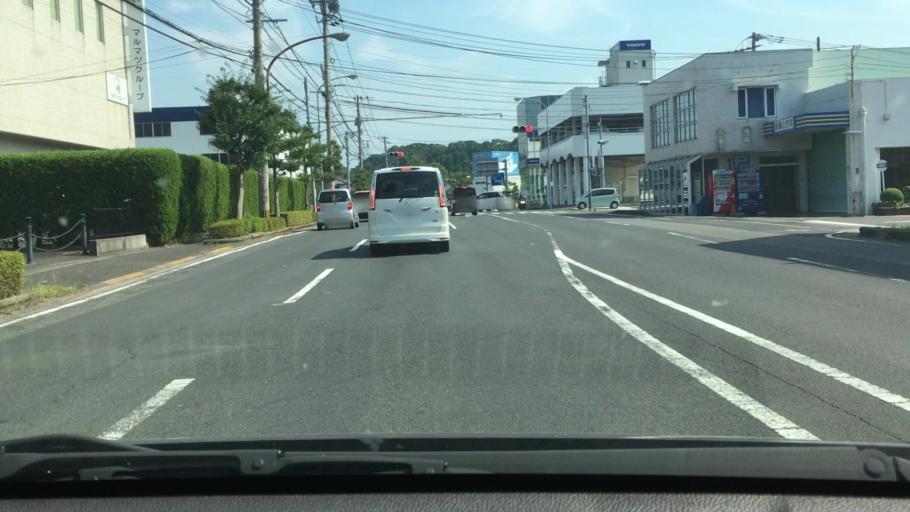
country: JP
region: Nagasaki
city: Sasebo
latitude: 33.1508
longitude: 129.7710
